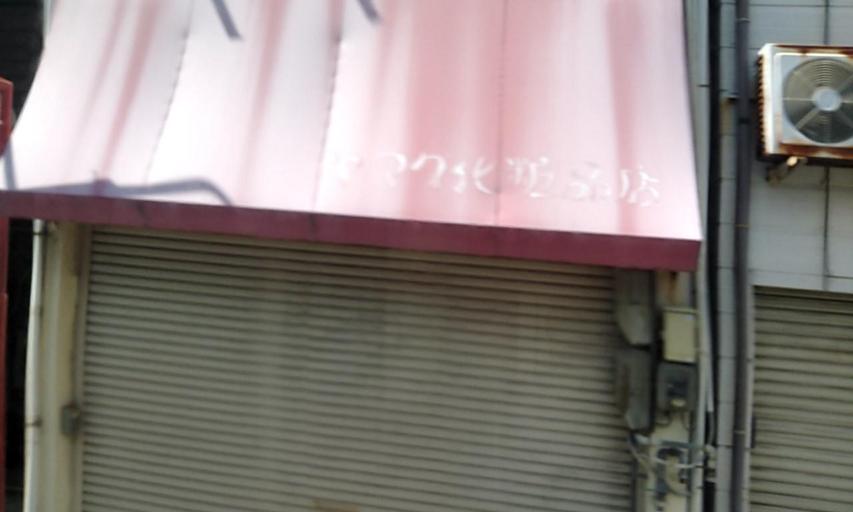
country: JP
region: Kagawa
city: Takamatsu-shi
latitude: 34.3373
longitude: 134.0520
